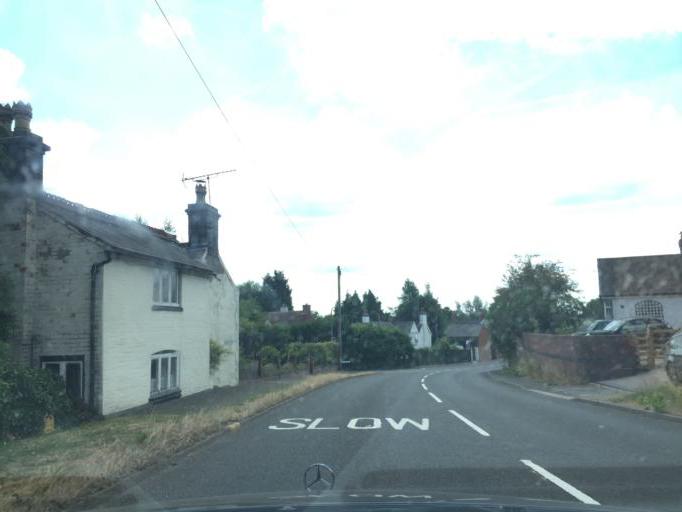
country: GB
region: England
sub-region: Warwickshire
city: Bedworth
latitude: 52.4580
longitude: -1.4031
